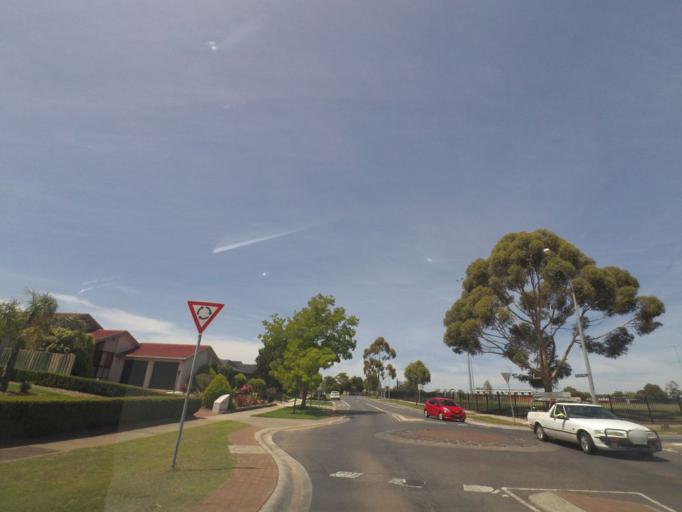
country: AU
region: Victoria
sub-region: Brimbank
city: Taylors Lakes
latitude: -37.7068
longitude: 144.7902
